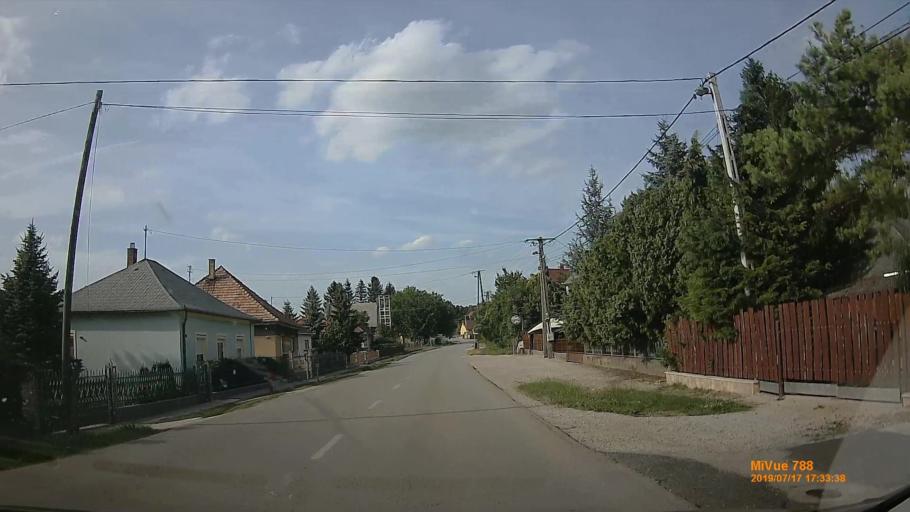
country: HU
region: Veszprem
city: Ajka
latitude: 47.0503
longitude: 17.5544
